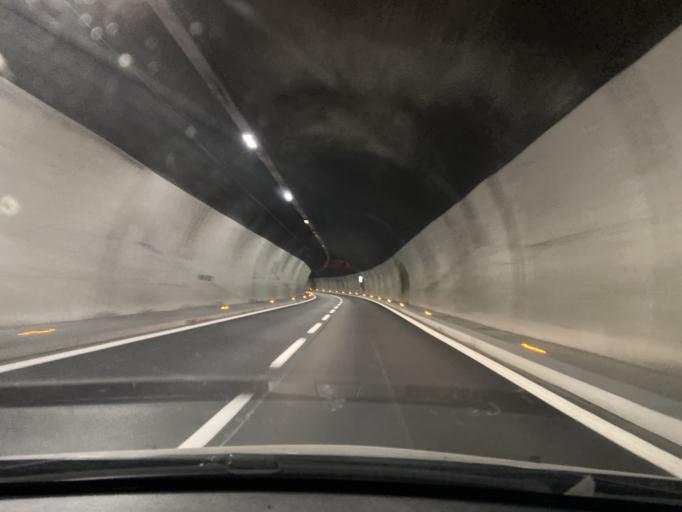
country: IT
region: Piedmont
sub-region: Provincia di Torino
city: Chiomonte
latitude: 45.1287
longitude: 6.9848
